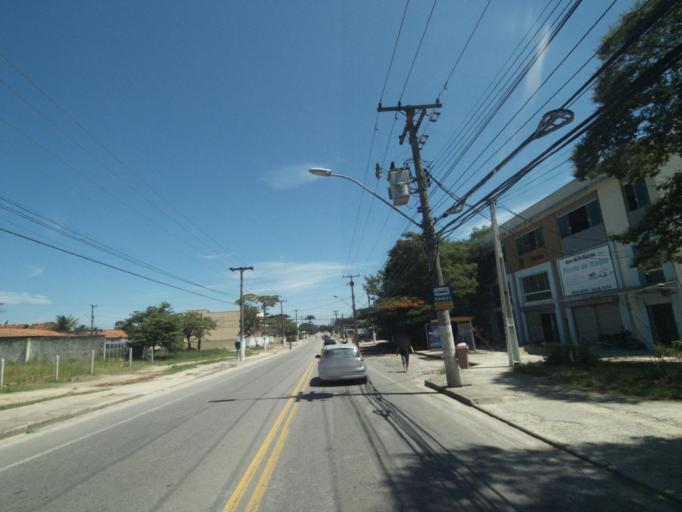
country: BR
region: Rio de Janeiro
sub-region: Niteroi
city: Niteroi
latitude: -22.9313
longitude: -43.0177
